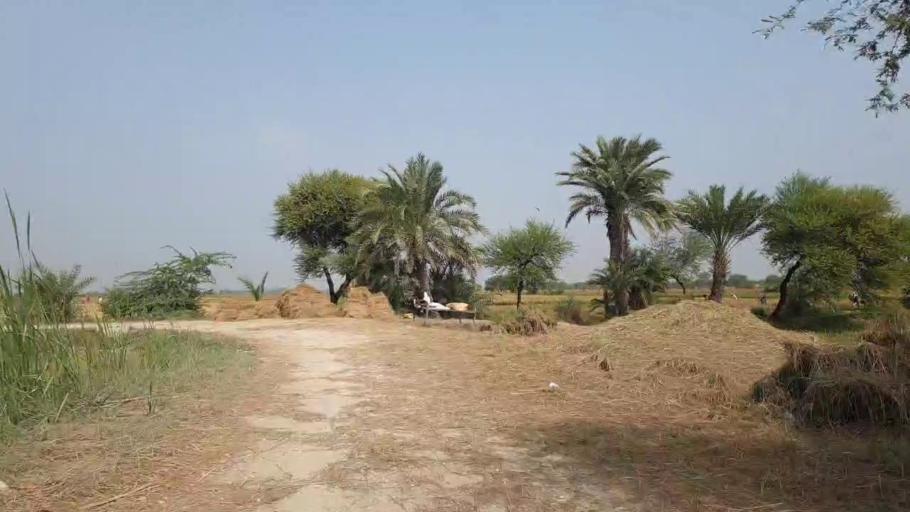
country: PK
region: Sindh
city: Kario
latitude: 24.7599
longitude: 68.5458
